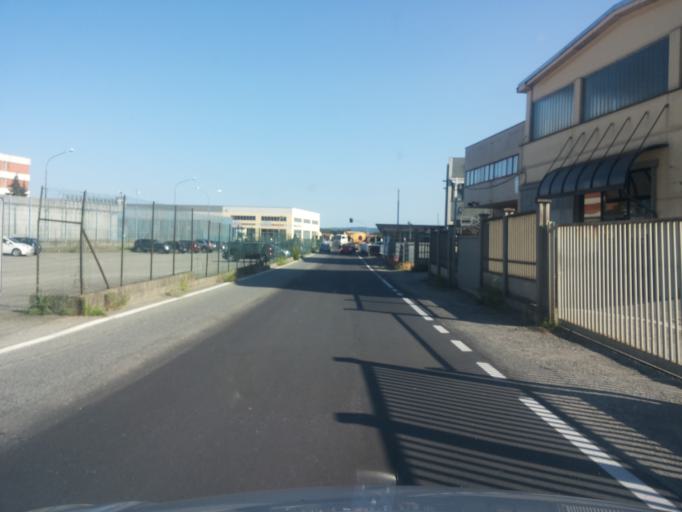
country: IT
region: Piedmont
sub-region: Provincia di Torino
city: Cascinette d'Ivrea
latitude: 45.4715
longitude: 7.9123
